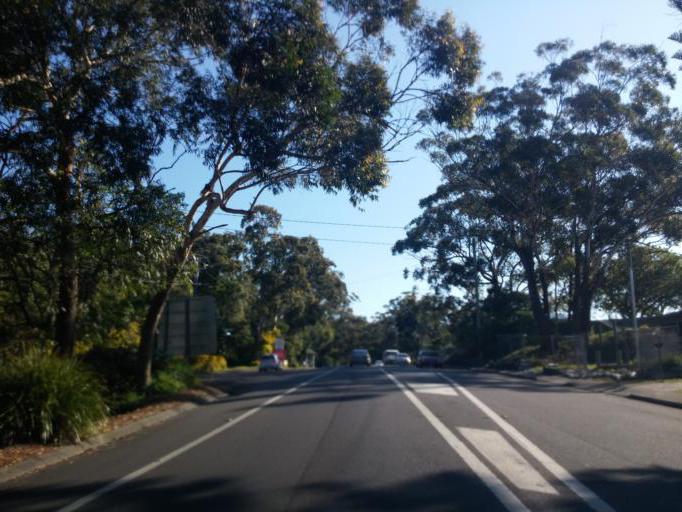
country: AU
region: New South Wales
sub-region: Port Stephens Shire
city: Nelson Bay
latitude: -32.7249
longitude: 152.1404
